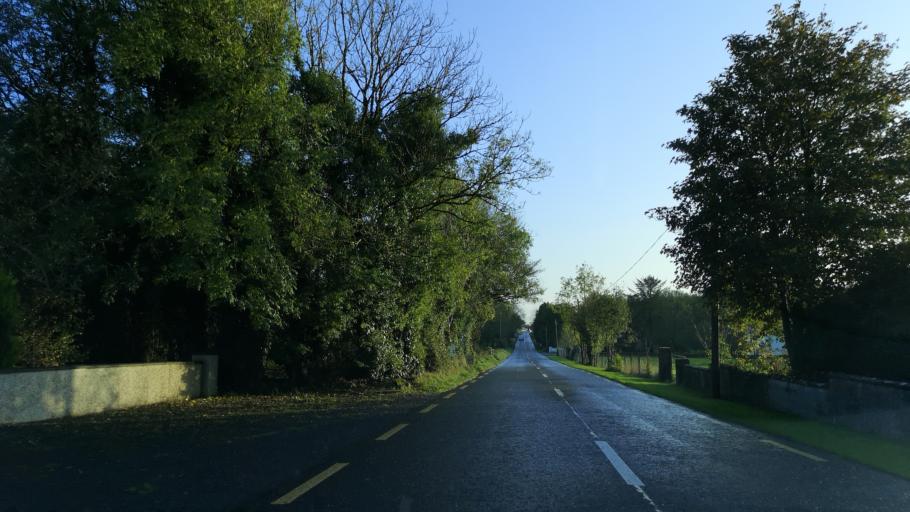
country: IE
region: Connaught
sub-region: Roscommon
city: Castlerea
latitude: 53.7224
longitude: -8.5588
